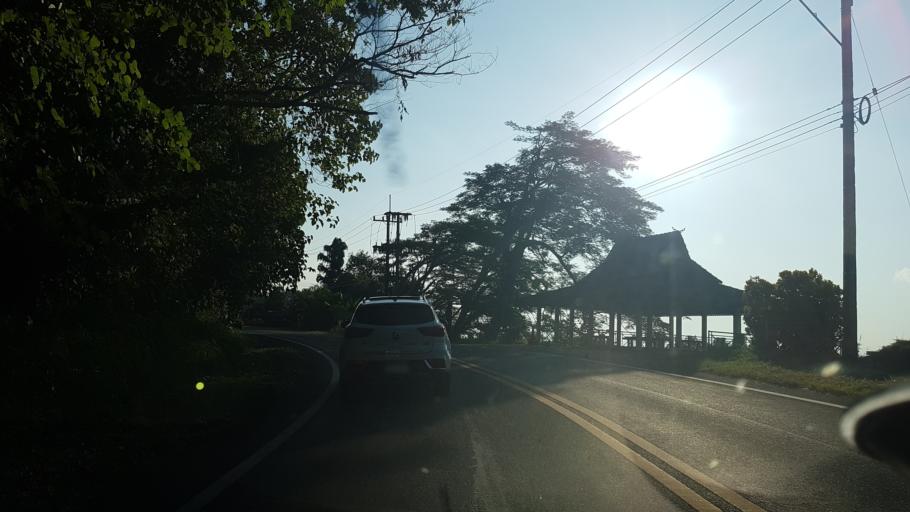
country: TH
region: Chiang Rai
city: Mae Fa Luang
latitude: 20.3073
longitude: 99.8171
